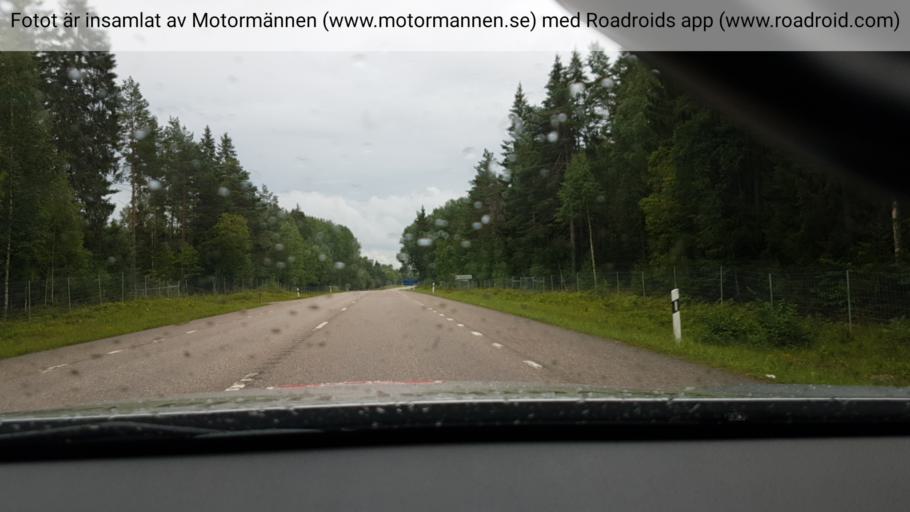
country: SE
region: Uppsala
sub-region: Alvkarleby Kommun
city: AElvkarleby
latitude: 60.5903
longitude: 17.4639
